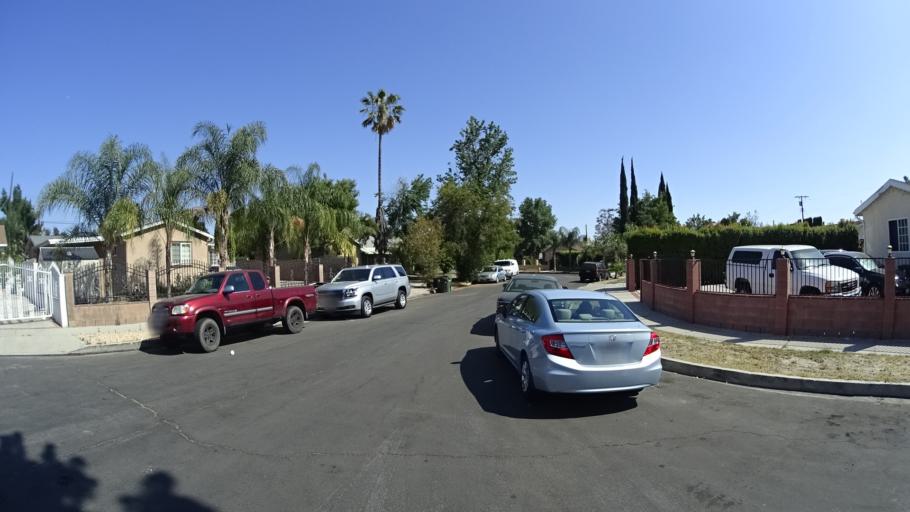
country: US
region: California
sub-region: Los Angeles County
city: Van Nuys
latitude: 34.2173
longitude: -118.4199
